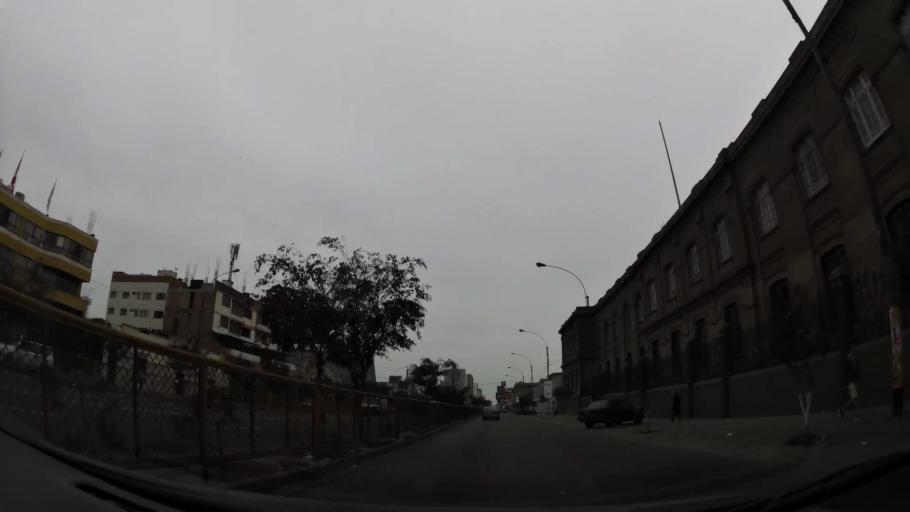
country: PE
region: Lima
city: Lima
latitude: -12.0617
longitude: -77.0427
